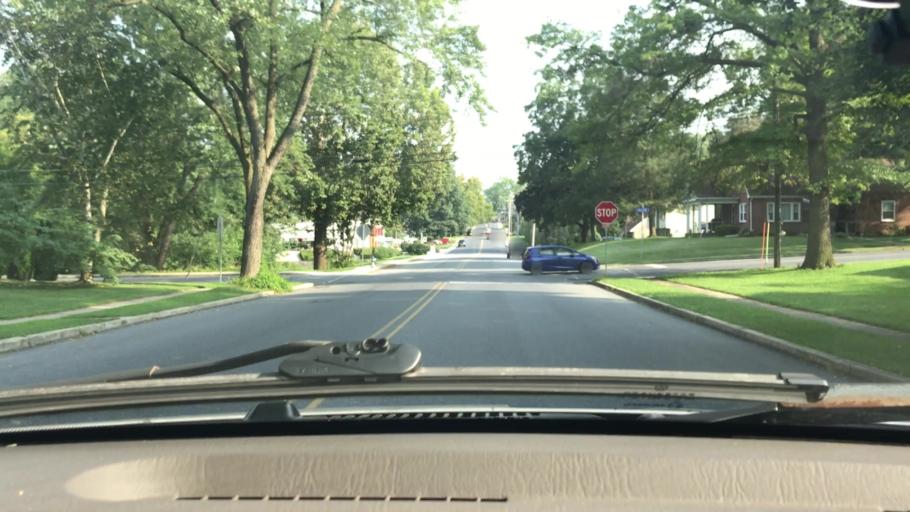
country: US
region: Pennsylvania
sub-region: Lancaster County
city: Elizabethtown
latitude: 40.1571
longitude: -76.6017
